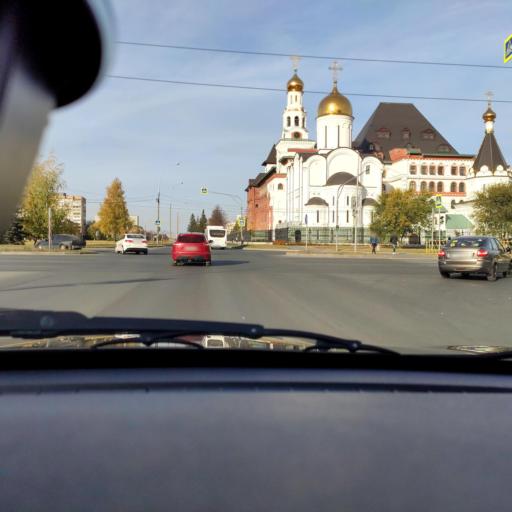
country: RU
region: Samara
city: Tol'yatti
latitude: 53.5292
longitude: 49.2823
